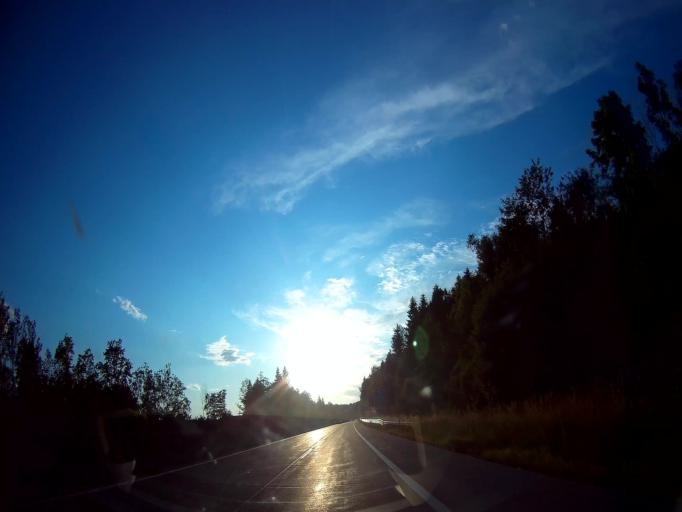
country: AT
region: Salzburg
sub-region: Politischer Bezirk Salzburg-Umgebung
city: Thalgau
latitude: 47.8504
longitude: 13.2319
